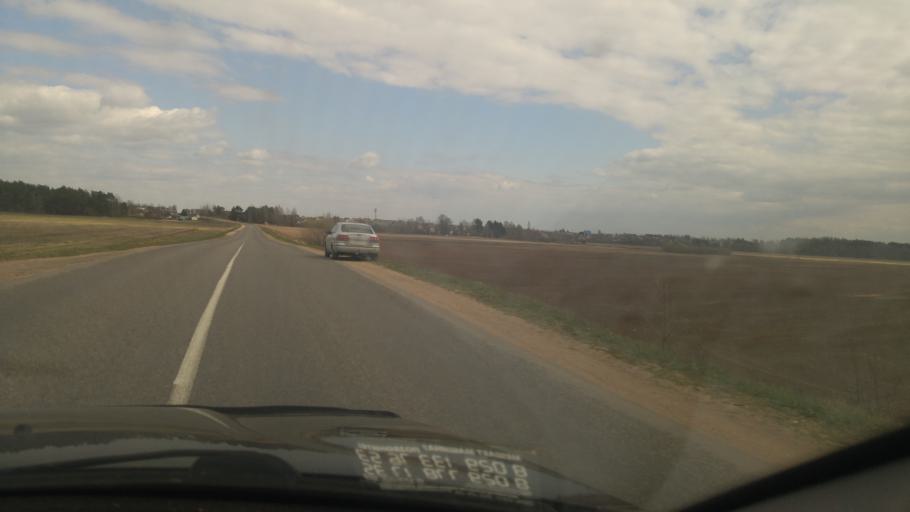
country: BY
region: Minsk
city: Rudzyensk
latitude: 53.6558
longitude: 27.8140
